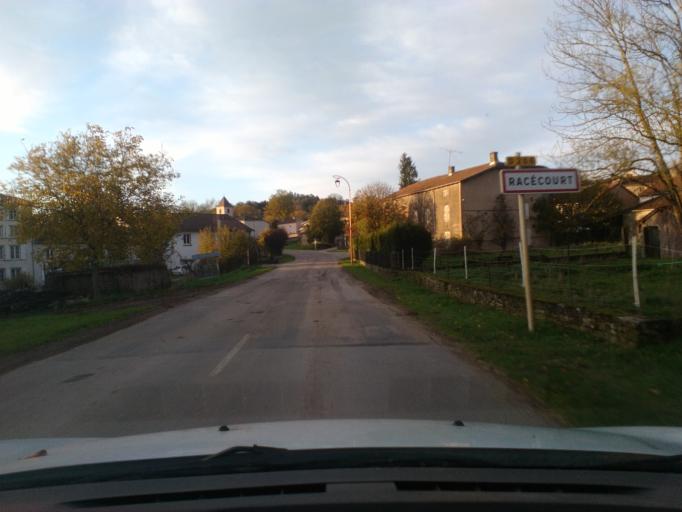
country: FR
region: Lorraine
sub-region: Departement des Vosges
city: Mirecourt
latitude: 48.2561
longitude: 6.1943
